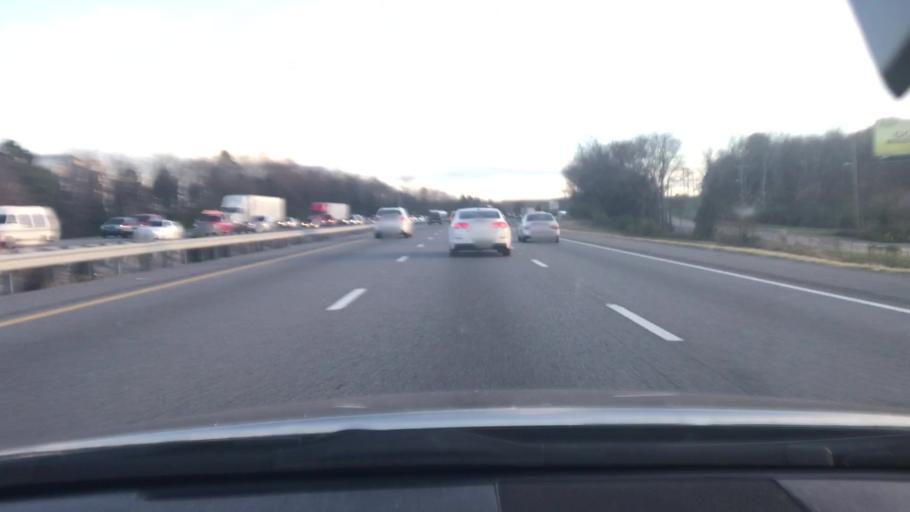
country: US
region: Tennessee
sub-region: Davidson County
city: Goodlettsville
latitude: 36.3184
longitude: -86.7025
